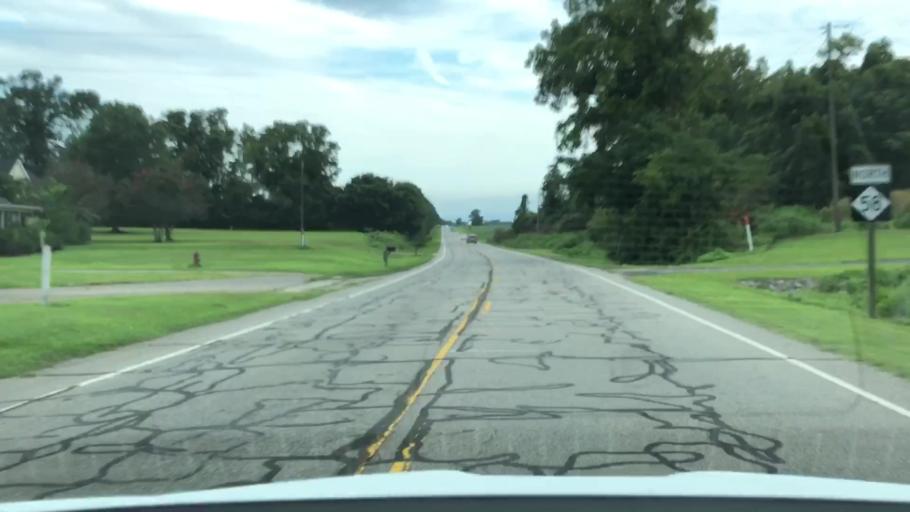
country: US
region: North Carolina
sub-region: Lenoir County
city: Kinston
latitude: 35.1385
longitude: -77.5297
